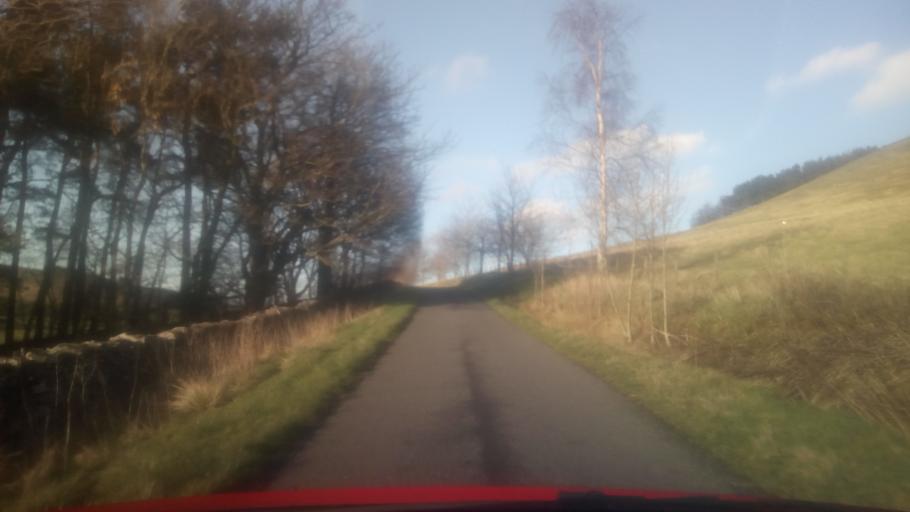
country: GB
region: Scotland
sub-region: The Scottish Borders
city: Kelso
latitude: 55.4505
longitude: -2.3627
